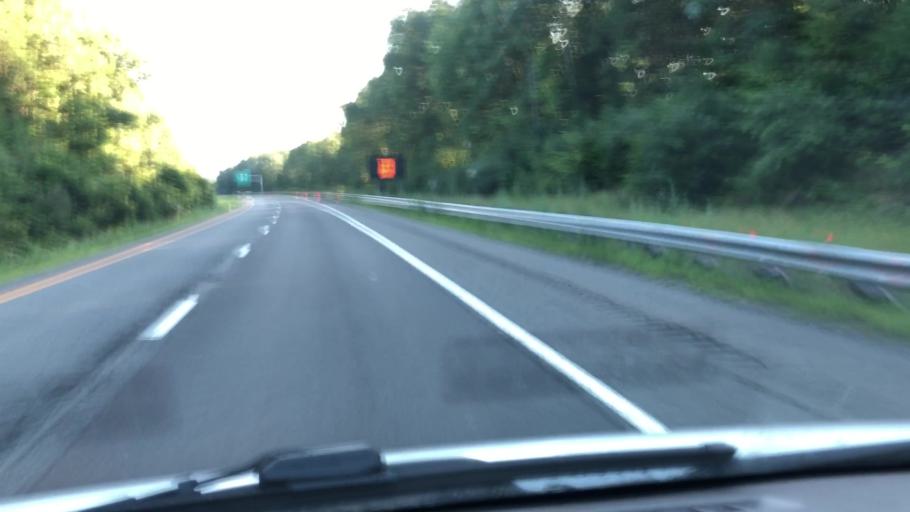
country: US
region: Massachusetts
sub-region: Franklin County
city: Greenfield
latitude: 42.5494
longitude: -72.6210
